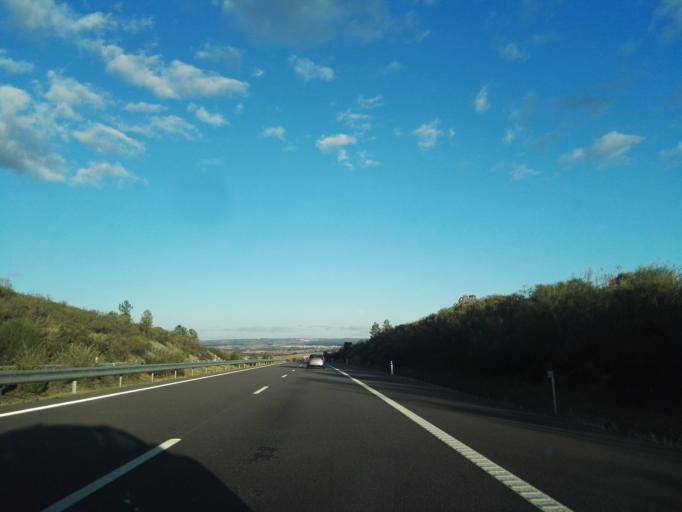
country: PT
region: Evora
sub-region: Borba
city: Borba
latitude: 38.8204
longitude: -7.4518
